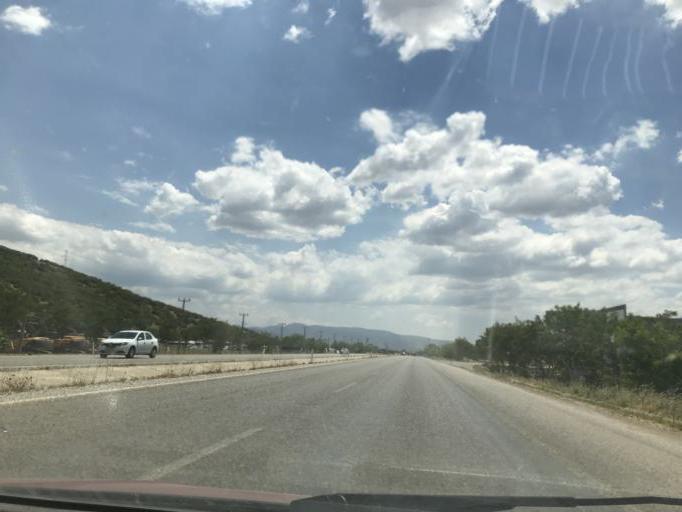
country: TR
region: Denizli
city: Tavas
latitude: 37.5567
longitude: 29.0561
